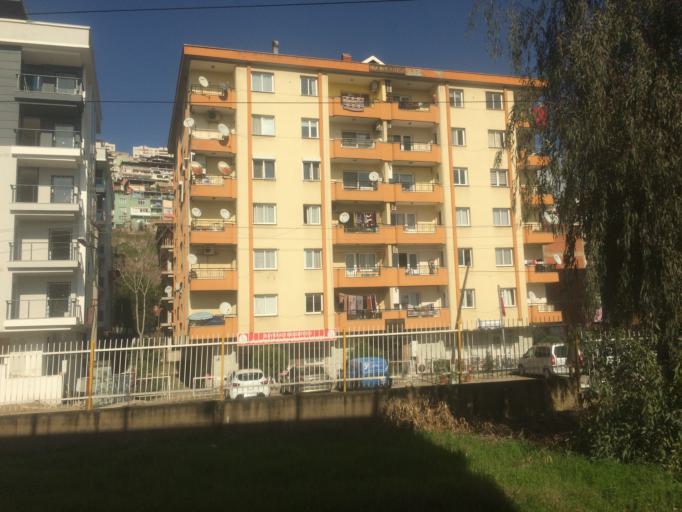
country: TR
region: Izmir
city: Karsiyaka
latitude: 38.4685
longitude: 27.1574
